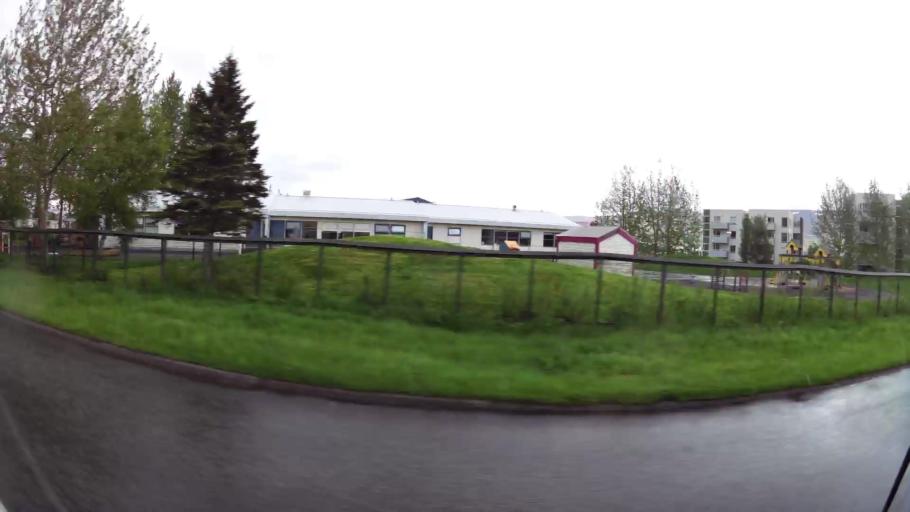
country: IS
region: Northeast
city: Akureyri
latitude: 65.6892
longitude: -18.1367
